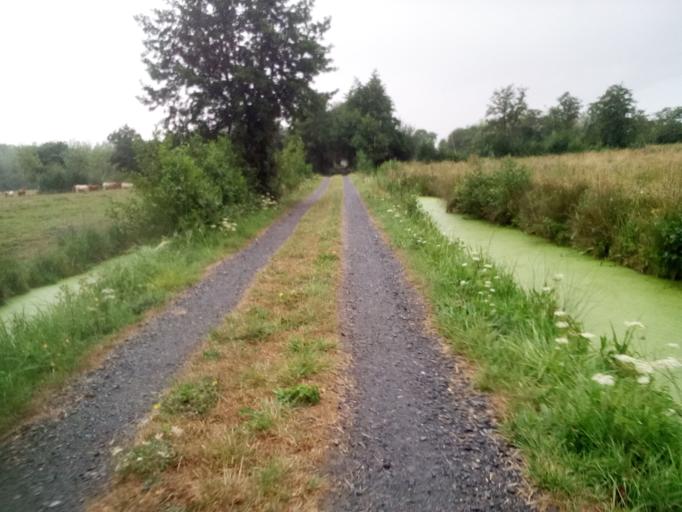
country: FR
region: Lower Normandy
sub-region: Departement du Calvados
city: Bavent
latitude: 49.2363
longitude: -0.1546
